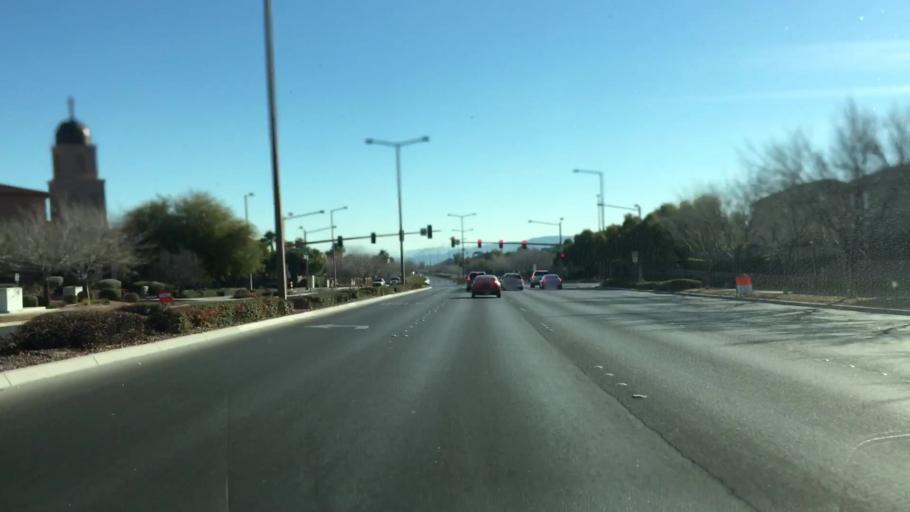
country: US
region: Nevada
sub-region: Clark County
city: Summerlin South
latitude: 36.1417
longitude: -115.3264
